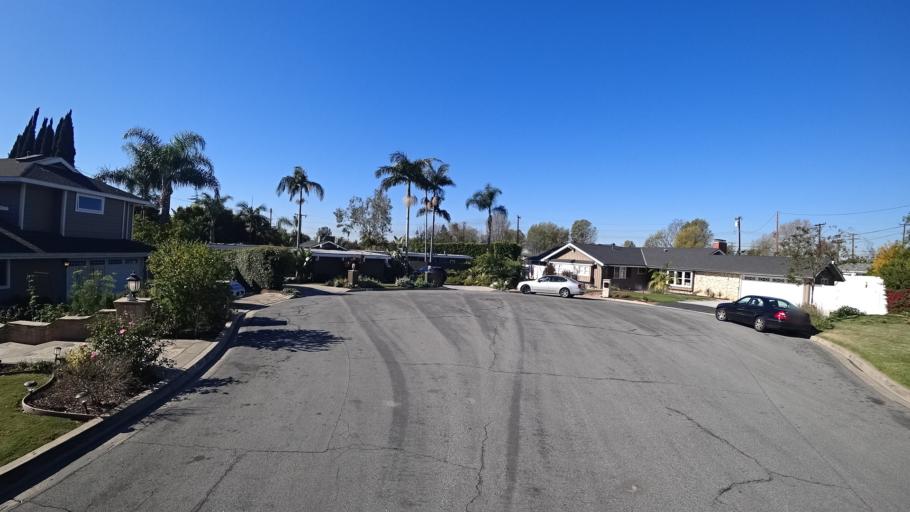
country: US
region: California
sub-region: Orange County
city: North Tustin
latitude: 33.7728
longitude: -117.8100
